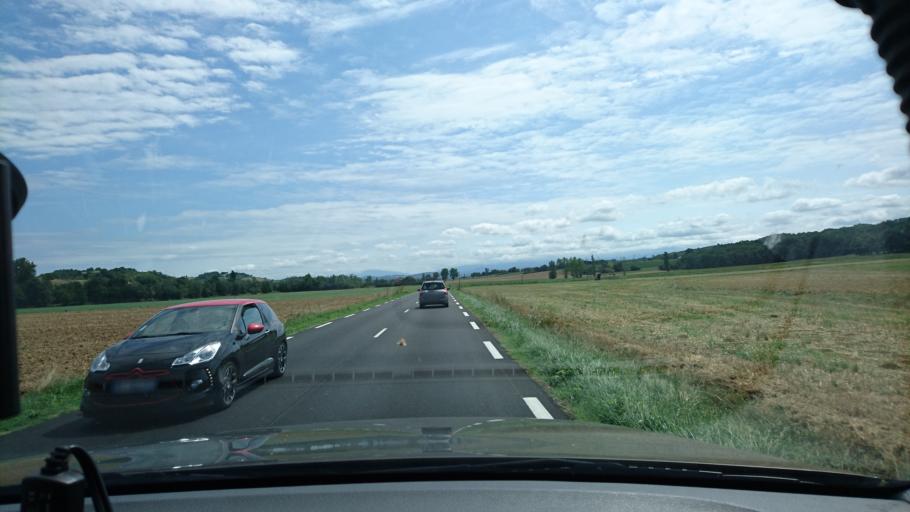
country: FR
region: Midi-Pyrenees
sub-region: Departement de l'Ariege
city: Lezat-sur-Leze
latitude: 43.2000
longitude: 1.3896
